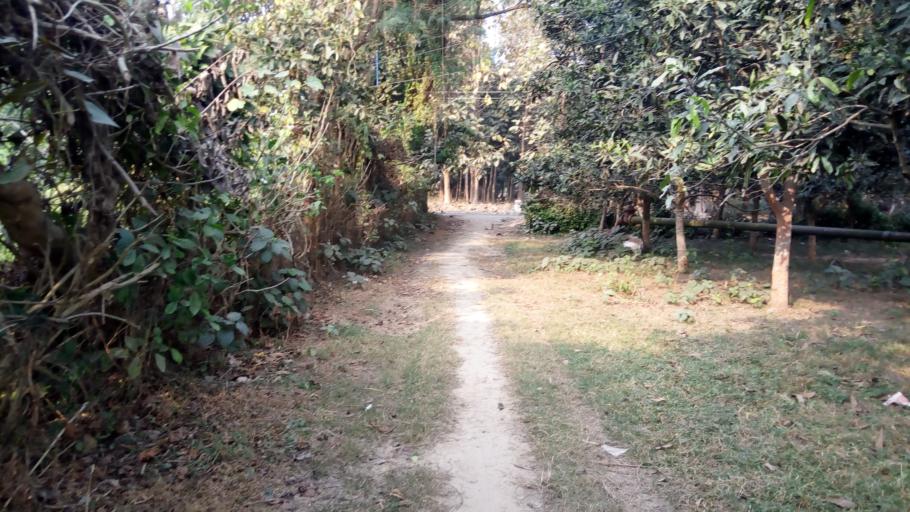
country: IN
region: West Bengal
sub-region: Nadia
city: Navadwip
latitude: 23.4471
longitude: 88.4179
